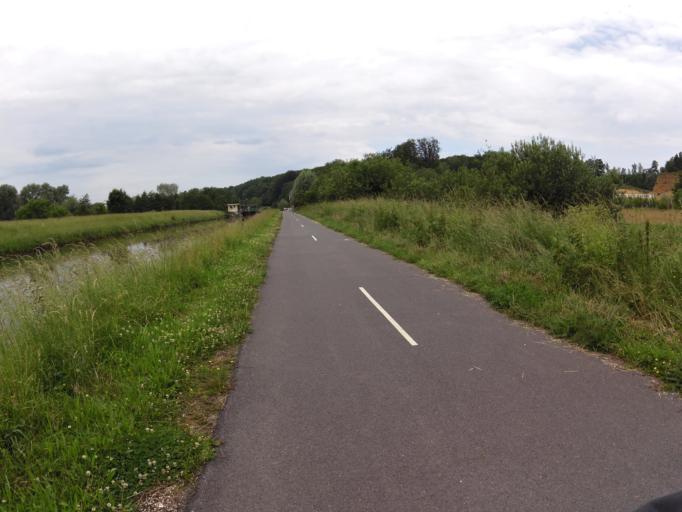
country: FR
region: Champagne-Ardenne
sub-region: Departement des Ardennes
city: Saint-Laurent
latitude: 49.7522
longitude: 4.7628
